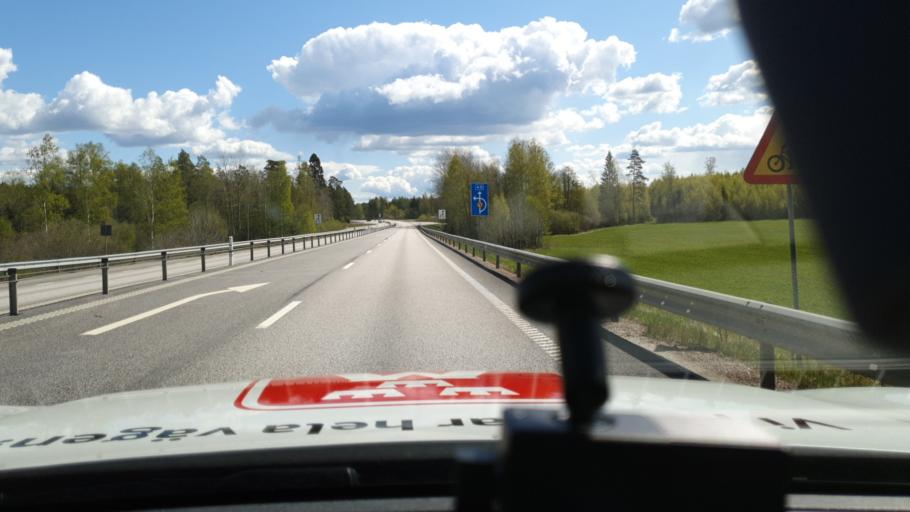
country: SE
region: Kalmar
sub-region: Vimmerby Kommun
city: Vimmerby
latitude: 57.7079
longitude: 16.0327
